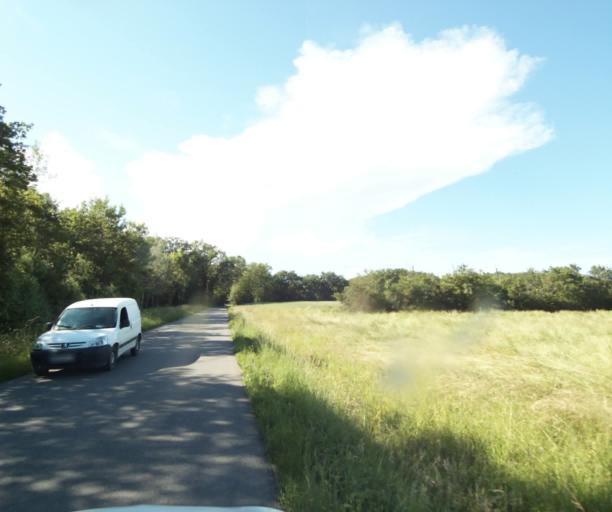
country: FR
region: Rhone-Alpes
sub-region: Departement de la Haute-Savoie
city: Massongy
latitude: 46.3308
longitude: 6.3292
